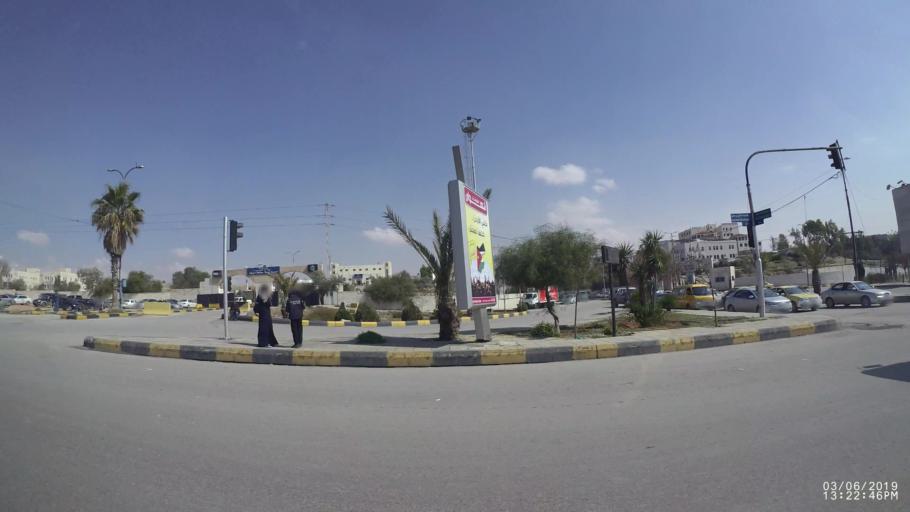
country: JO
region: Zarqa
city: Zarqa
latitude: 32.0516
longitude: 36.0934
